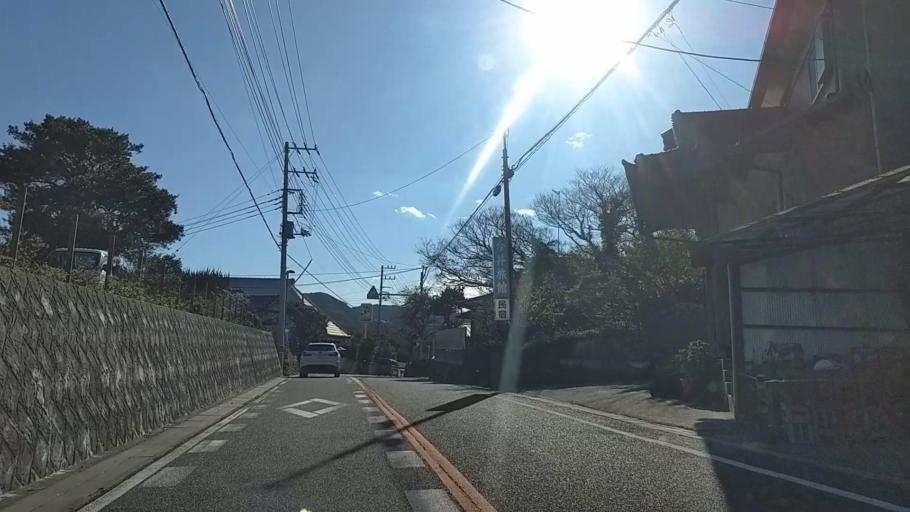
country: JP
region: Chiba
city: Futtsu
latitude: 35.1472
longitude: 139.8322
